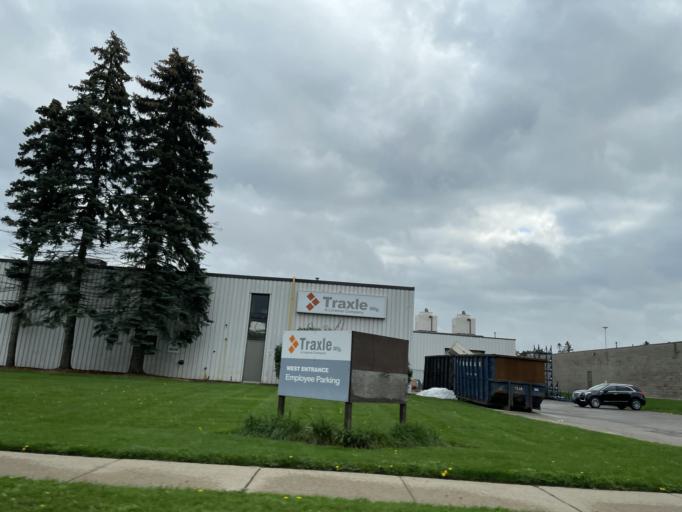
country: CA
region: Ontario
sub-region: Wellington County
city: Guelph
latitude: 43.5458
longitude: -80.2855
